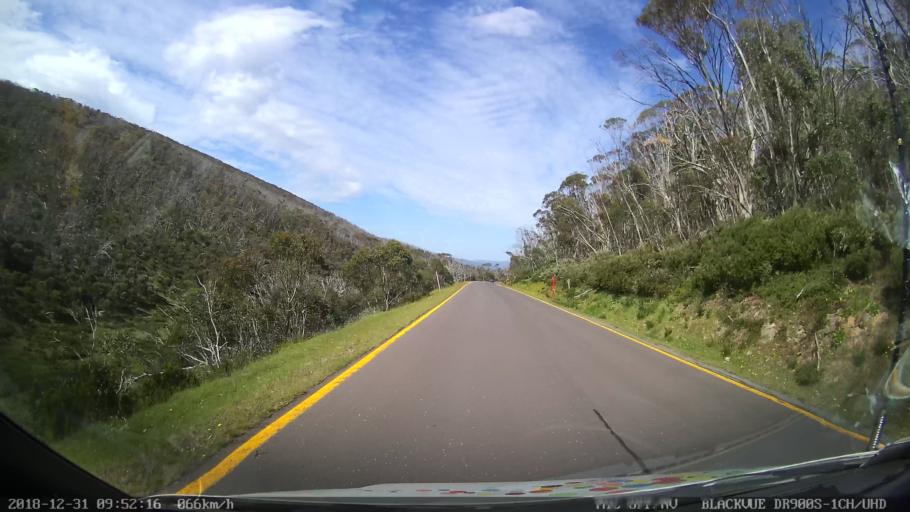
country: AU
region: New South Wales
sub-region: Snowy River
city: Jindabyne
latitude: -36.5263
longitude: 148.2548
